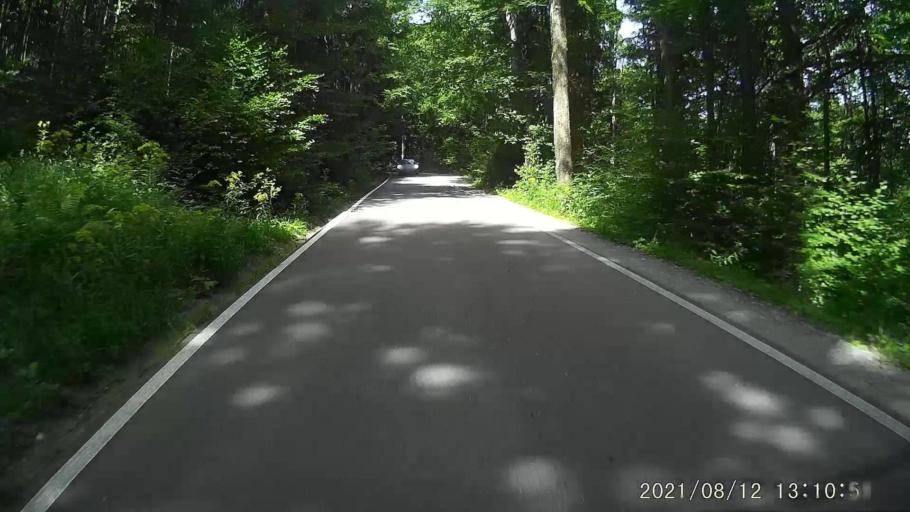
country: PL
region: Lower Silesian Voivodeship
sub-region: Powiat klodzki
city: Stronie Slaskie
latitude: 50.2451
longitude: 16.8502
